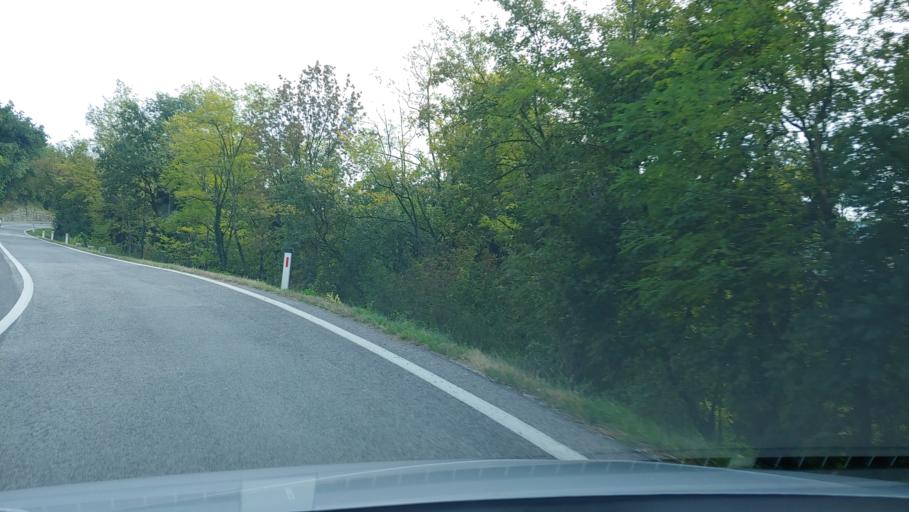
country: SI
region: Nova Gorica
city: Sempas
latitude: 45.9034
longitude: 13.7791
